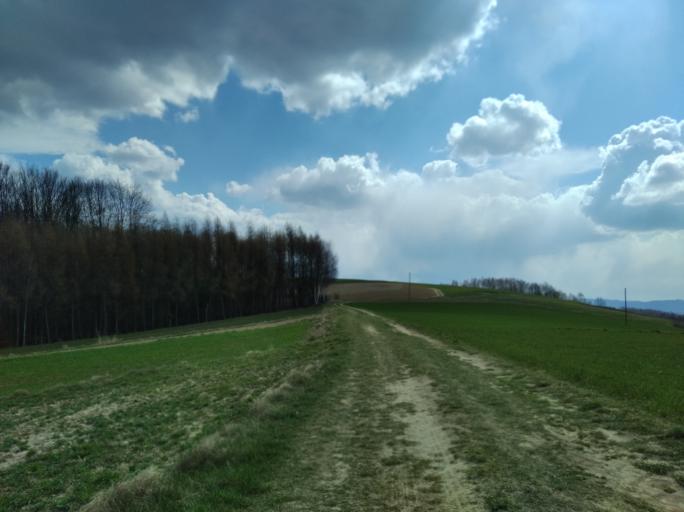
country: PL
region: Subcarpathian Voivodeship
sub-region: Powiat strzyzowski
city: Strzyzow
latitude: 49.9144
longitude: 21.7471
